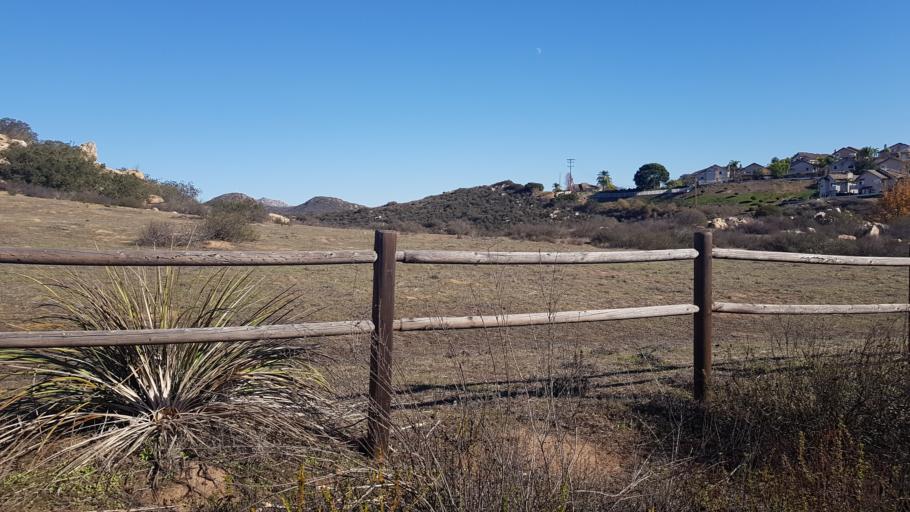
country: US
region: California
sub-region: San Diego County
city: Escondido
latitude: 33.0452
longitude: -117.0896
